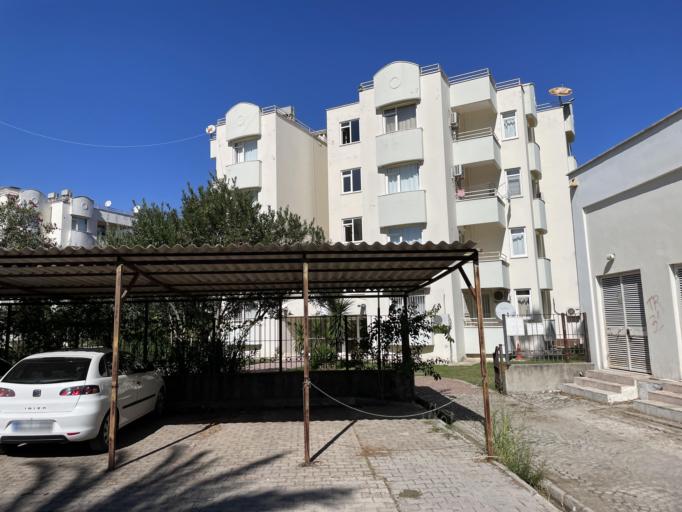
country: TR
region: Antalya
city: Kemer
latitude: 36.5958
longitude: 30.5659
